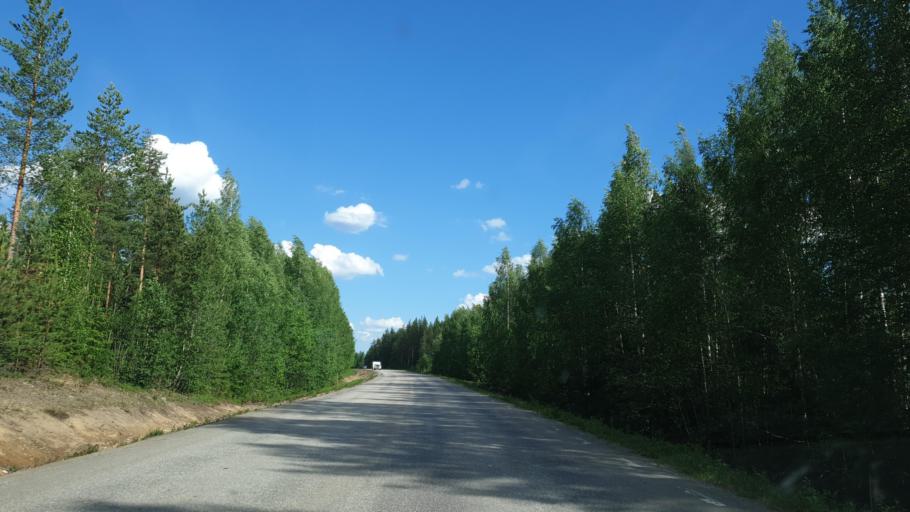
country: SE
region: Norrbotten
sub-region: Alvsbyns Kommun
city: AElvsbyn
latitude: 65.8482
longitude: 20.4611
